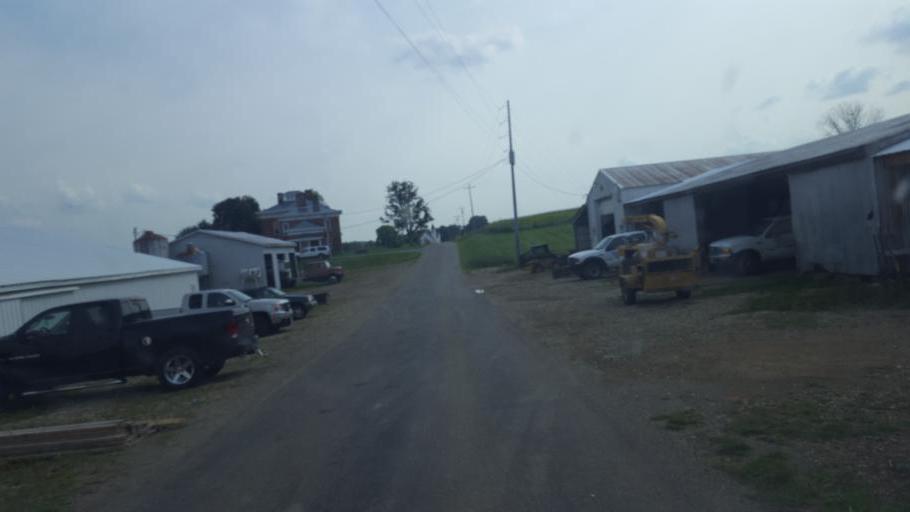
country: US
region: Ohio
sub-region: Knox County
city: Gambier
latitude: 40.3400
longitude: -82.3881
